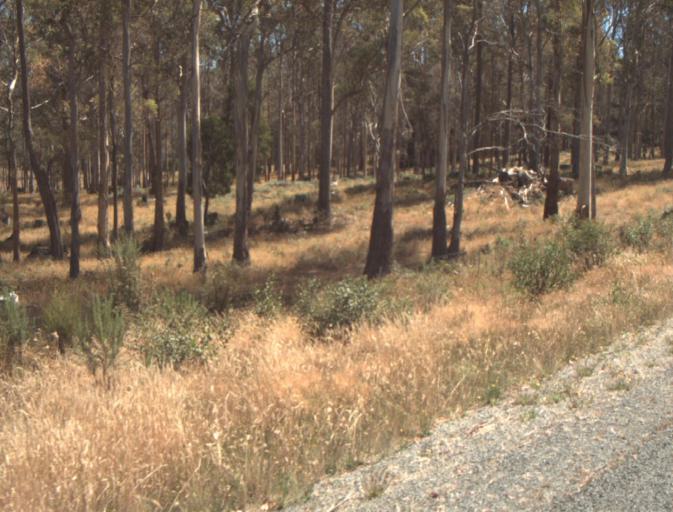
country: AU
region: Tasmania
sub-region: Launceston
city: Newstead
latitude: -41.3377
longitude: 147.3474
